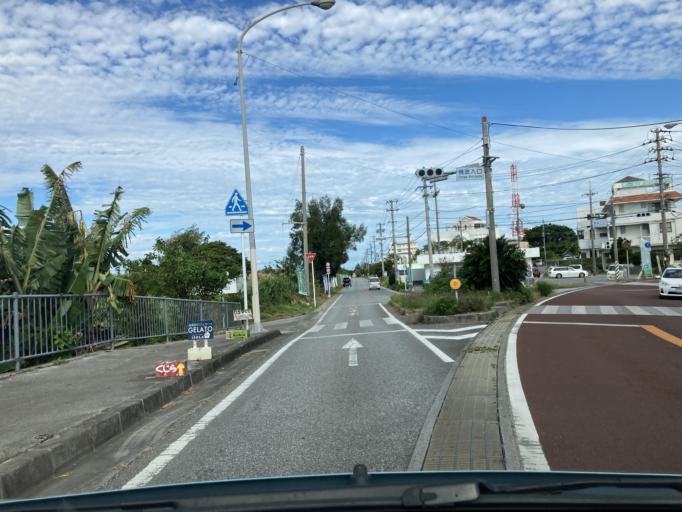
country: JP
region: Okinawa
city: Ishikawa
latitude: 26.4238
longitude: 127.7304
